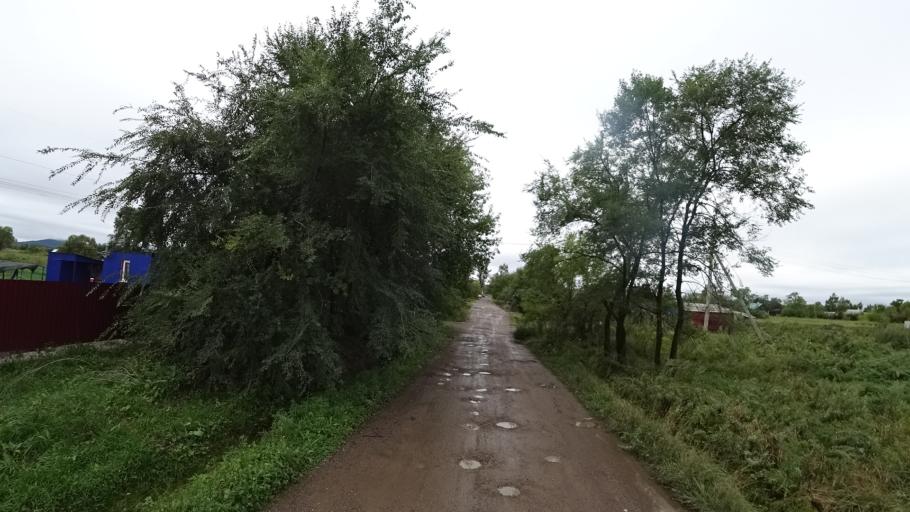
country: RU
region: Primorskiy
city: Monastyrishche
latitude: 44.1992
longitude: 132.4722
